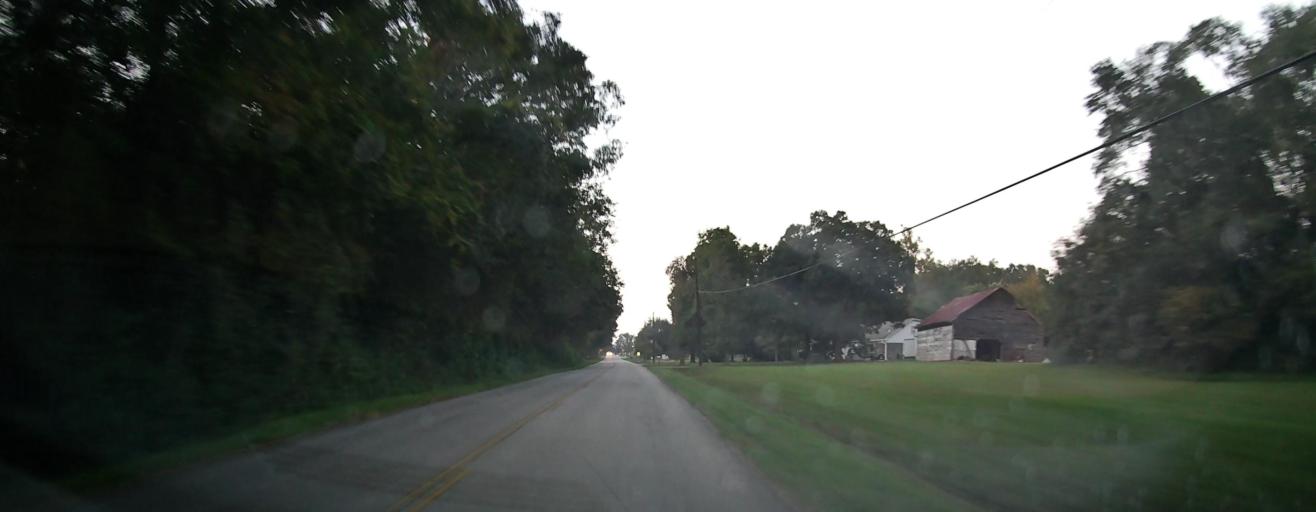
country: US
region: Georgia
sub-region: Henry County
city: Locust Grove
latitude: 33.3164
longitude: -84.0429
